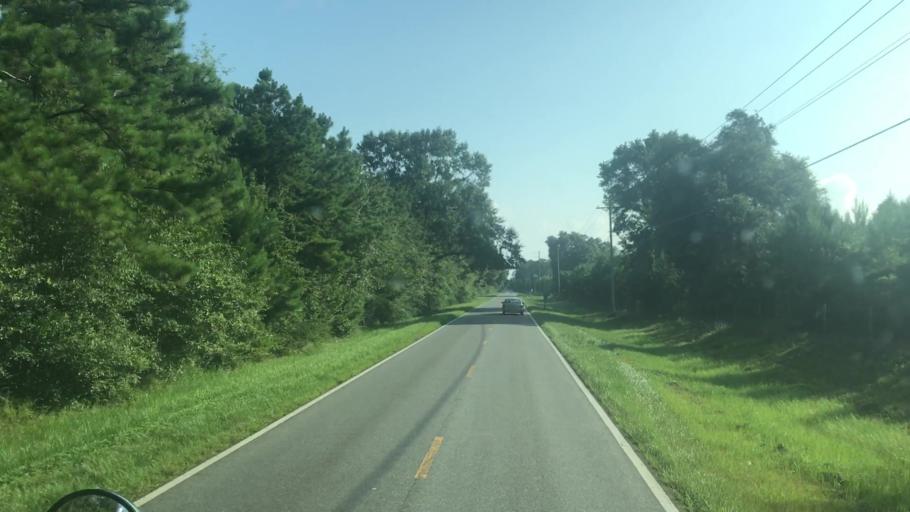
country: US
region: Florida
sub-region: Gadsden County
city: Quincy
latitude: 30.6392
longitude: -84.5754
